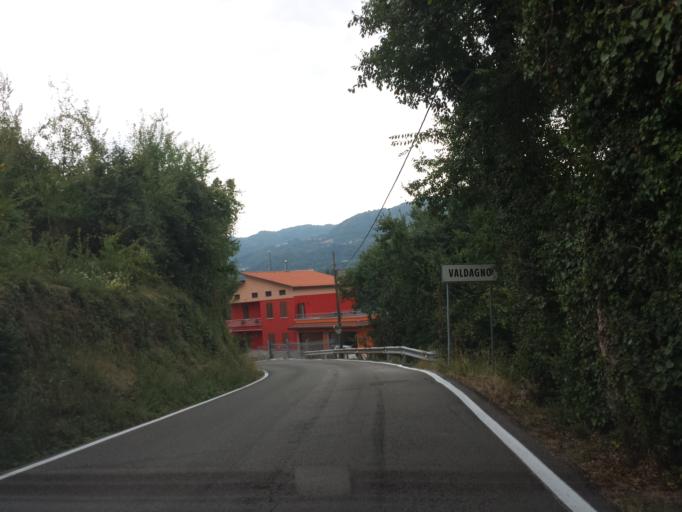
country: IT
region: Veneto
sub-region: Provincia di Vicenza
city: Valdagno
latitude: 45.6337
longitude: 11.3111
